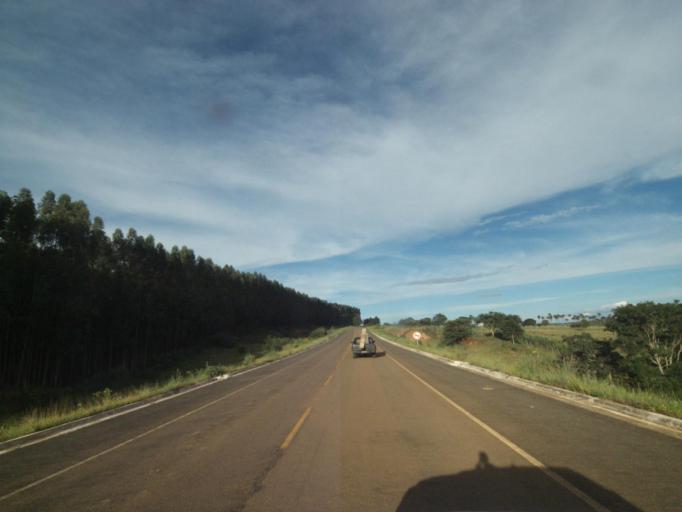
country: BR
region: Goias
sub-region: Jaragua
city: Jaragua
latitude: -15.8836
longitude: -49.4466
